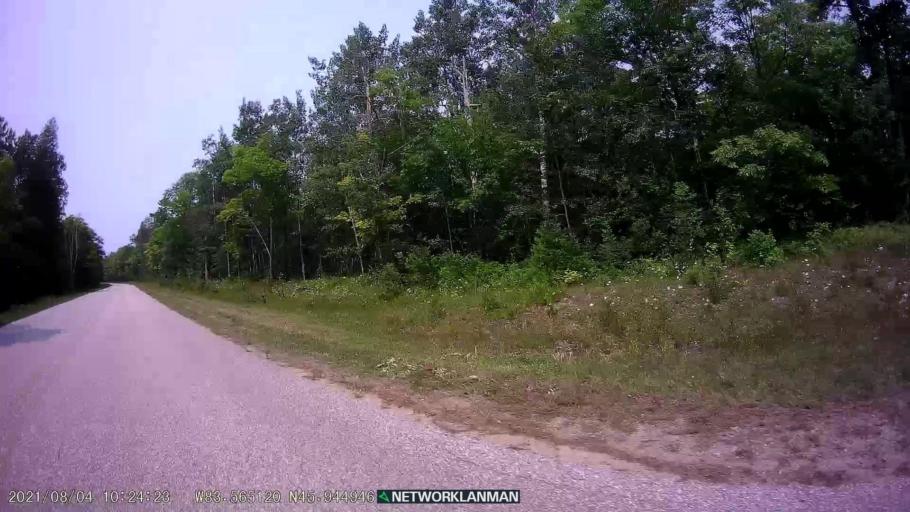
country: CA
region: Ontario
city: Thessalon
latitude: 45.9450
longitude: -83.5654
